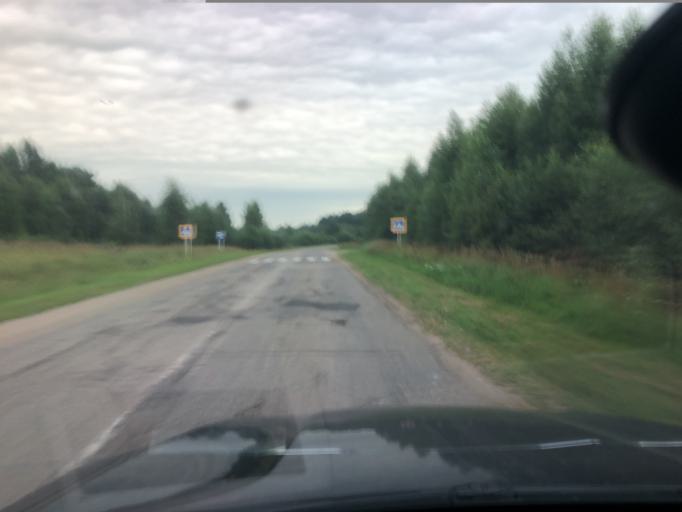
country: RU
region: Jaroslavl
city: Petrovsk
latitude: 57.0132
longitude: 38.9898
